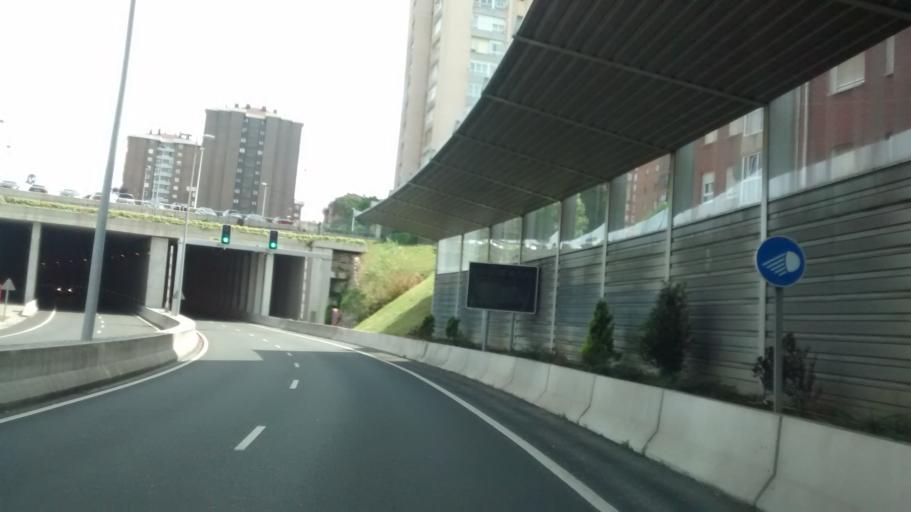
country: ES
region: Cantabria
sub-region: Provincia de Cantabria
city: Santander
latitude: 43.4604
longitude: -3.8358
